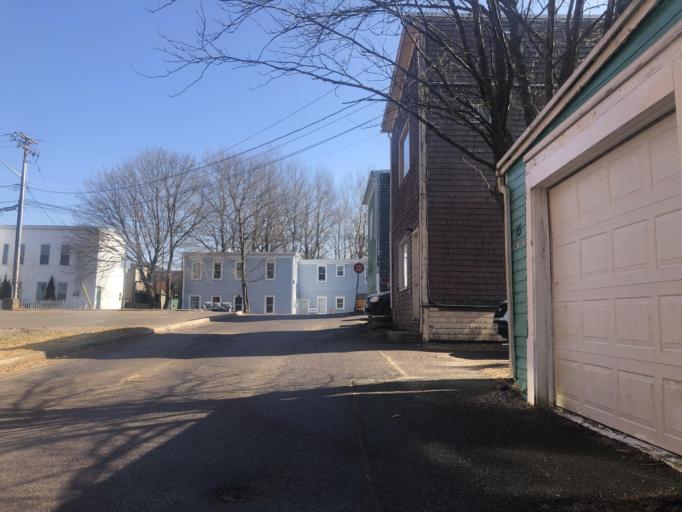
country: CA
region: New Brunswick
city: Saint John
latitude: 45.2754
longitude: -66.0866
